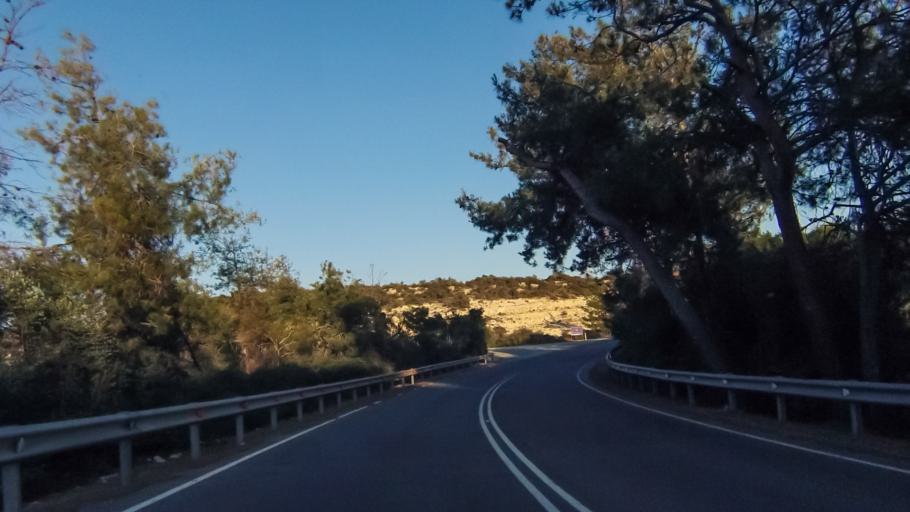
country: CY
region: Limassol
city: Sotira
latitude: 34.6763
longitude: 32.8509
